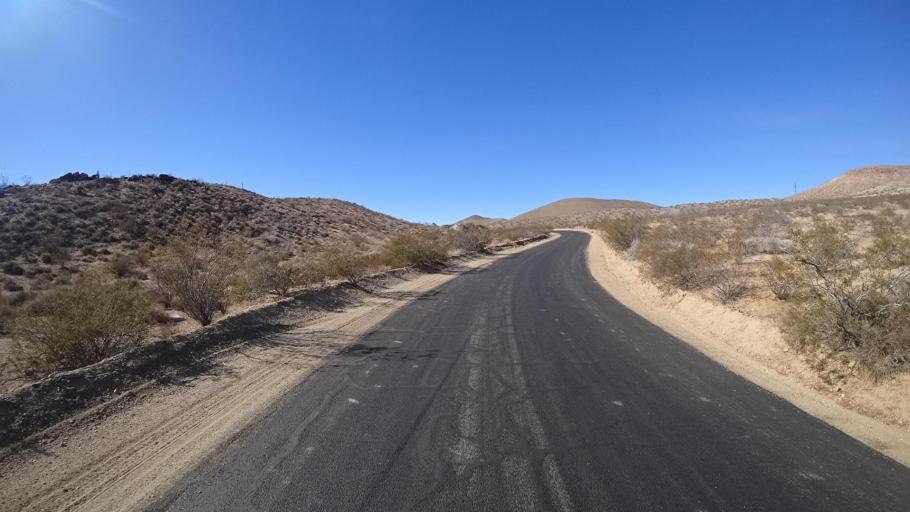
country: US
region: California
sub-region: Kern County
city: Ridgecrest
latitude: 35.3527
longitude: -117.6282
